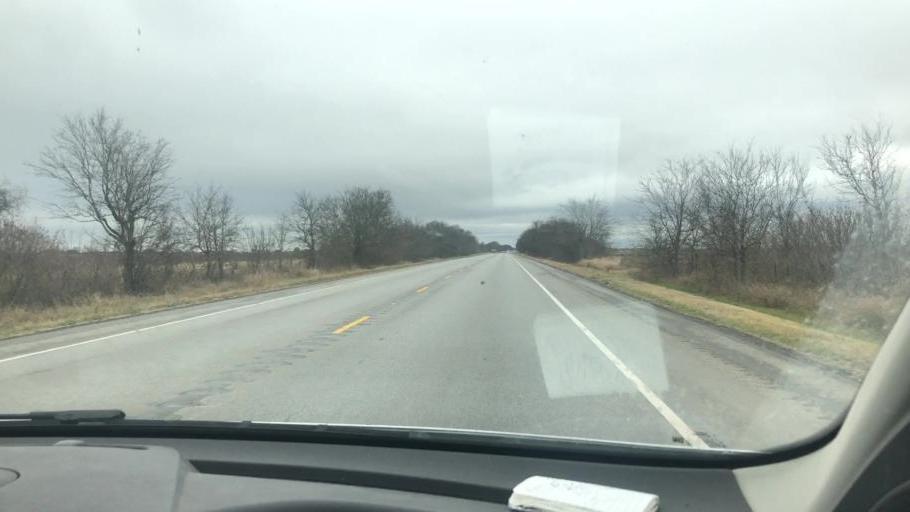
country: US
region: Texas
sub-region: Matagorda County
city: Van Vleck
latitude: 29.1230
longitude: -95.9815
